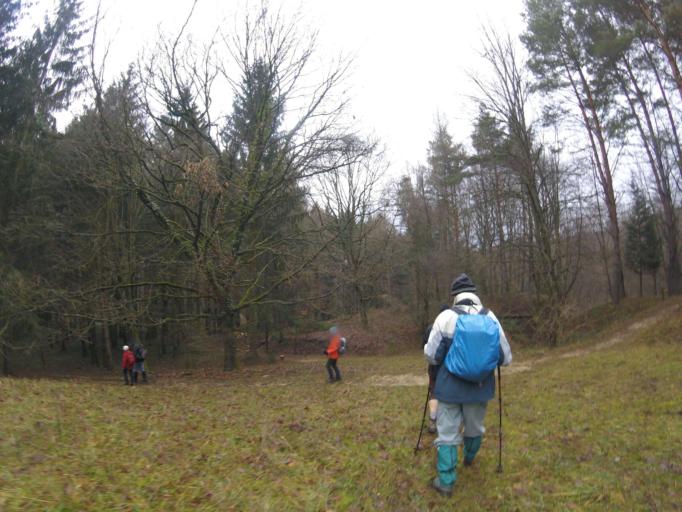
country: HU
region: Pest
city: Visegrad
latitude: 47.7715
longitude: 18.9857
